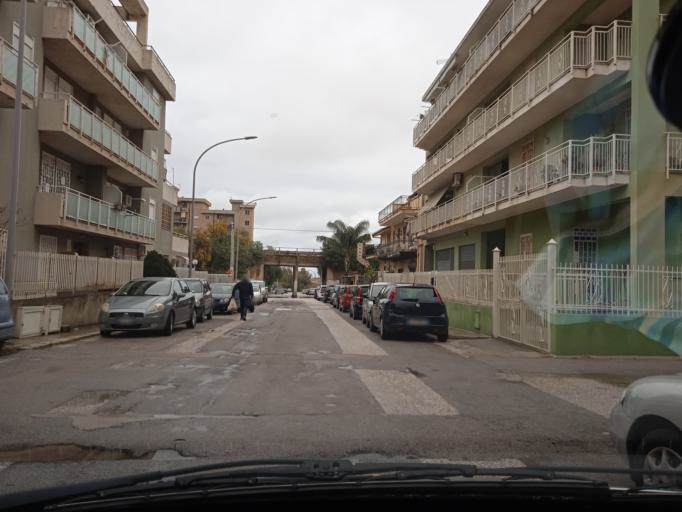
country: IT
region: Sicily
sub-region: Palermo
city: Villabate
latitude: 38.0797
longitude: 13.4442
